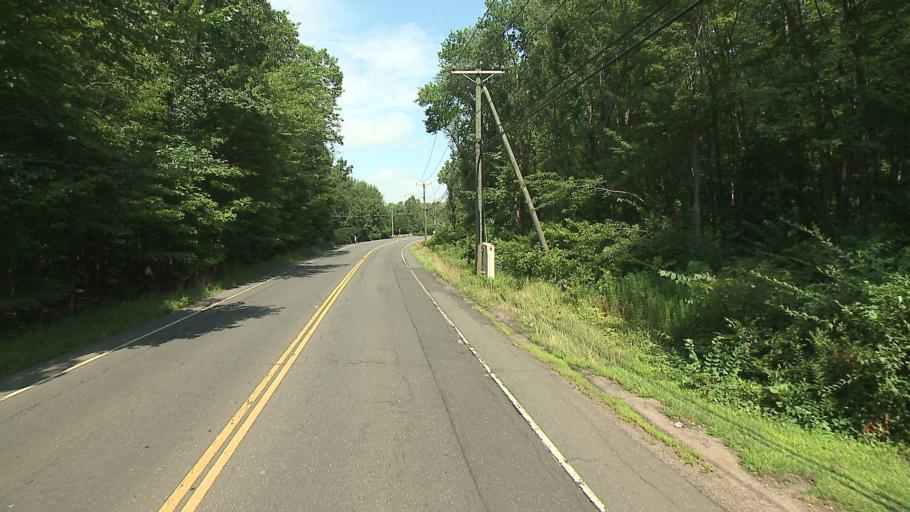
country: US
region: Connecticut
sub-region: Hartford County
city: Farmington
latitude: 41.7203
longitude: -72.8848
